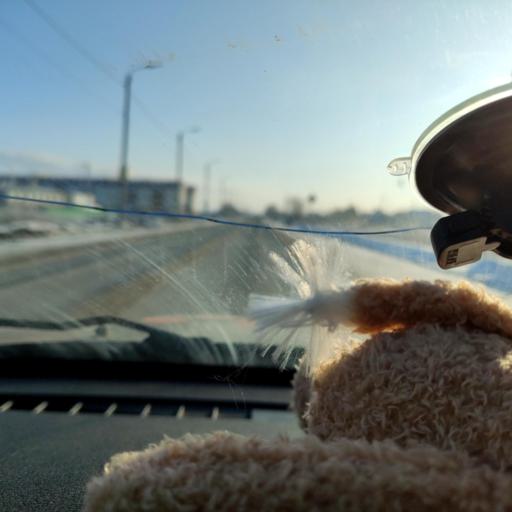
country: RU
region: Samara
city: Podstepki
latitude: 53.5205
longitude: 49.1852
